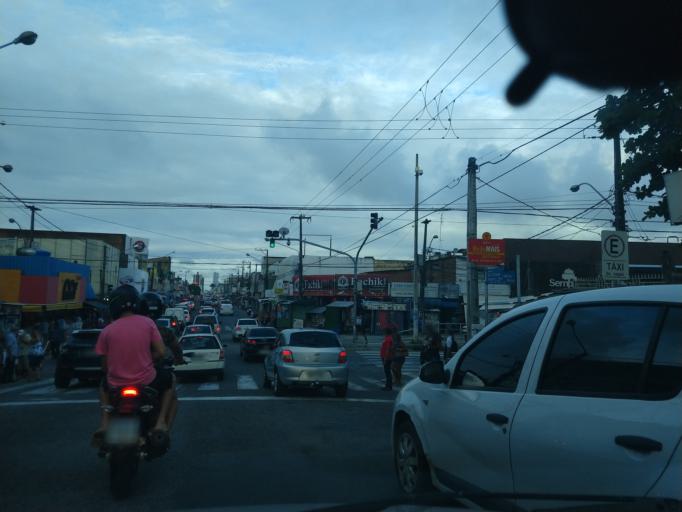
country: BR
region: Rio Grande do Norte
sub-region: Natal
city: Natal
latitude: -5.7971
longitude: -35.2179
